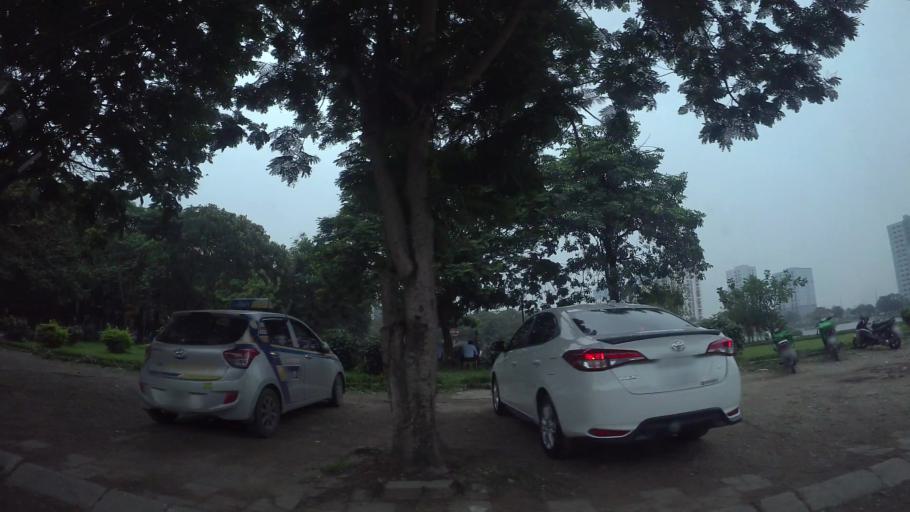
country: VN
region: Ha Noi
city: Hai BaTrung
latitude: 20.9862
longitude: 105.8545
